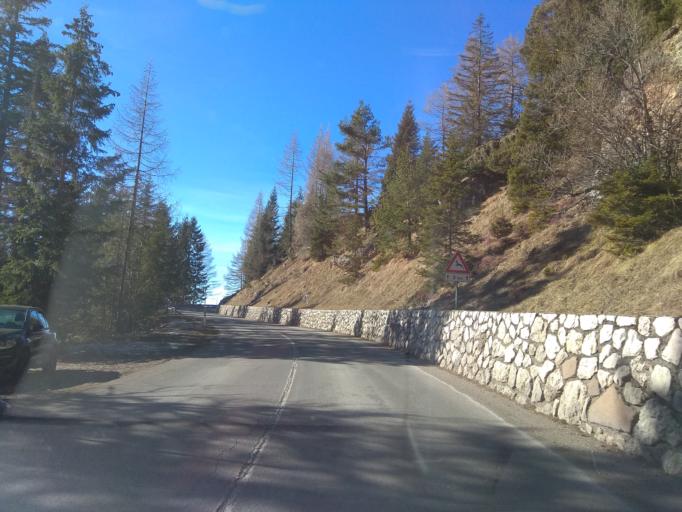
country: IT
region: Trentino-Alto Adige
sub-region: Bolzano
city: Nova Levante
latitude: 46.4239
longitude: 11.5979
